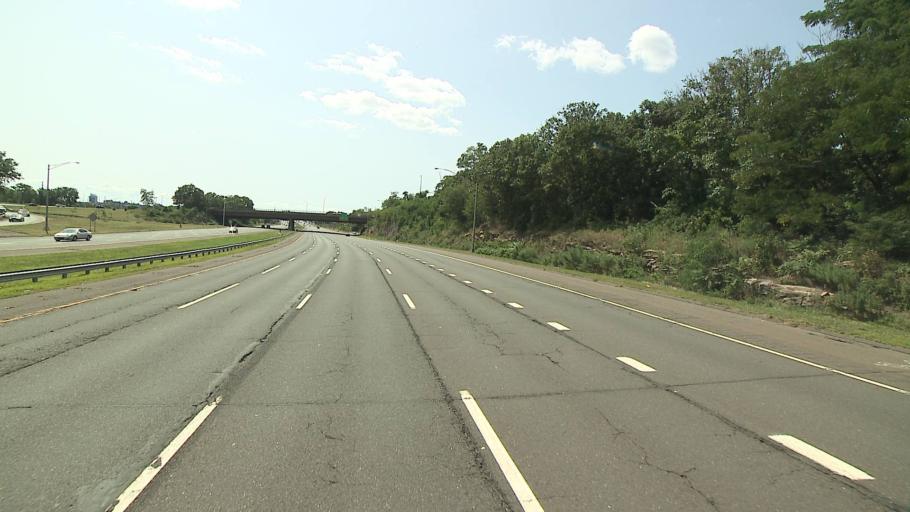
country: US
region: Connecticut
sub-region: Fairfield County
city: Trumbull
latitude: 41.2085
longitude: -73.1899
